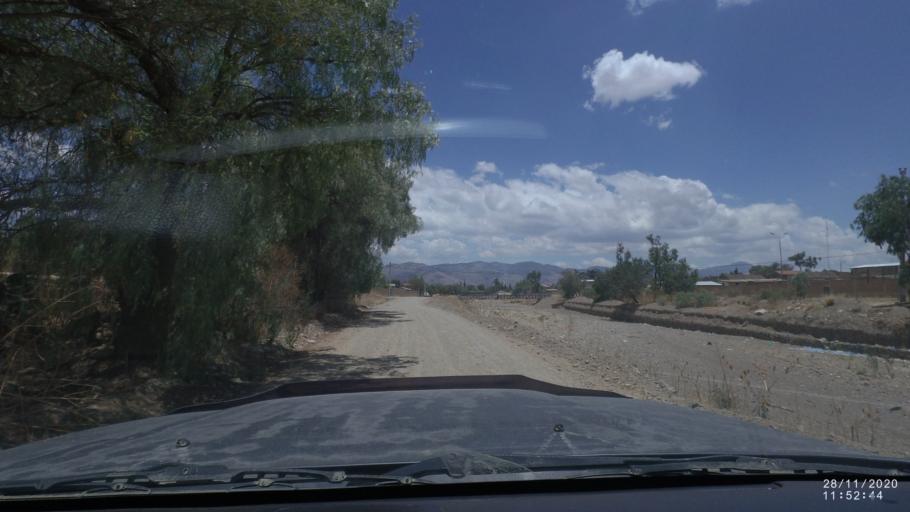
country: BO
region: Cochabamba
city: Tarata
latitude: -17.6143
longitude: -66.0216
